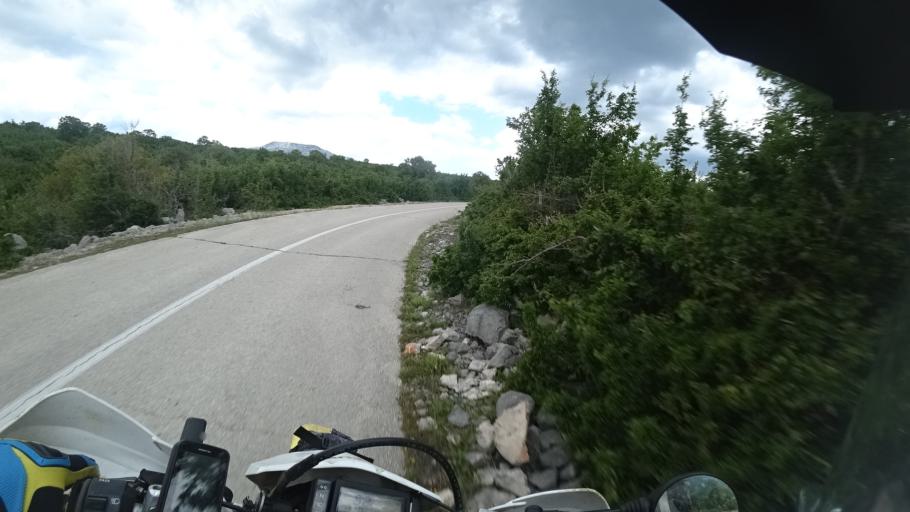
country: HR
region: Zadarska
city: Gracac
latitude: 44.1970
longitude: 15.8737
